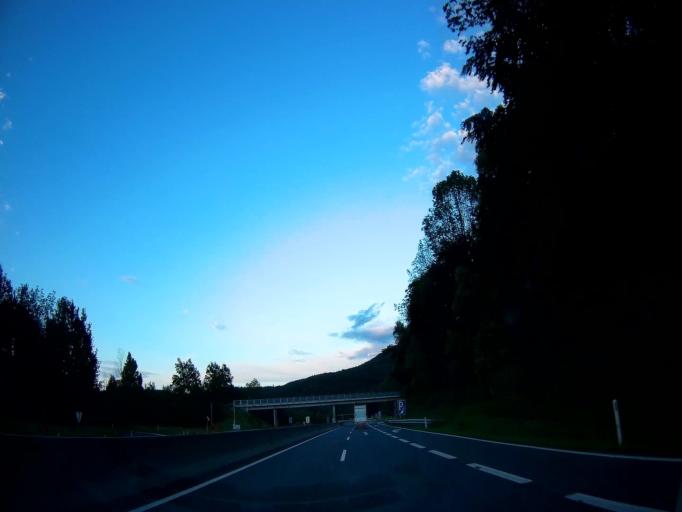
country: AT
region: Lower Austria
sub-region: Politischer Bezirk Sankt Polten
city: Eichgraben
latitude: 48.1616
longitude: 16.0039
